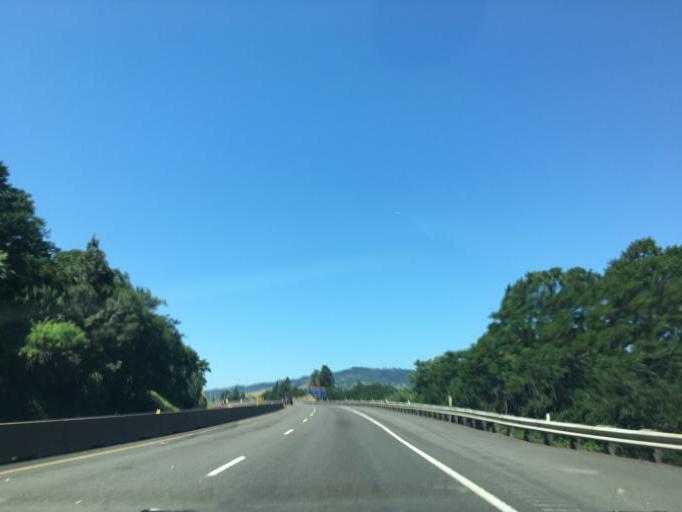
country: US
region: Oregon
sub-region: Wasco County
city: Chenoweth
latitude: 45.6946
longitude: -121.3330
